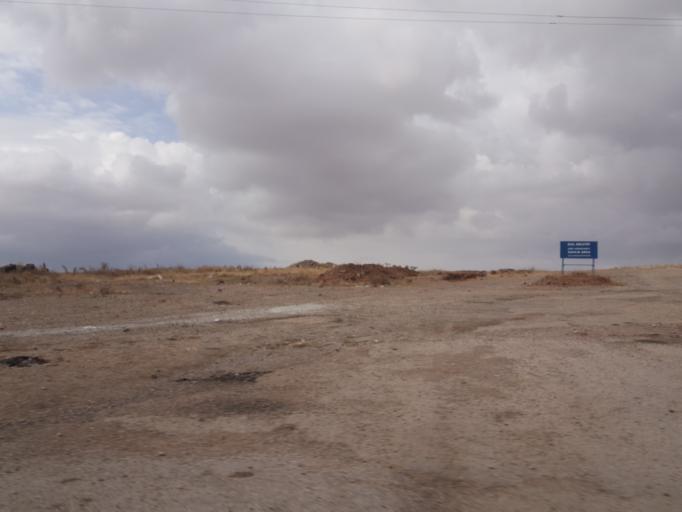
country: TR
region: Kirikkale
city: Keskin
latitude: 39.6561
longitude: 33.6174
